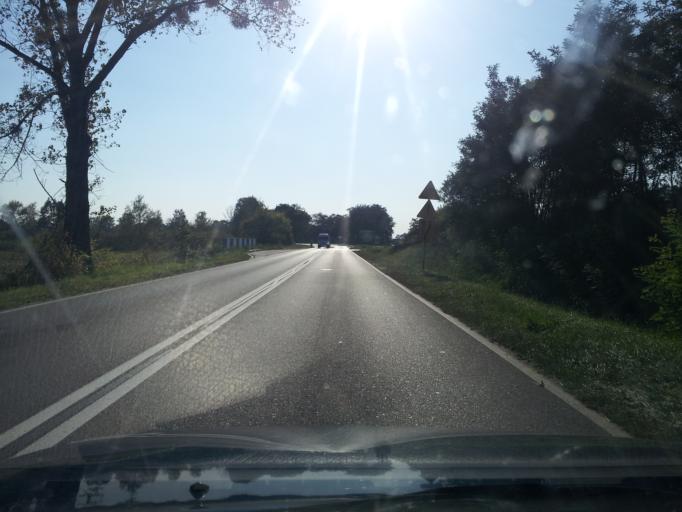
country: PL
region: Masovian Voivodeship
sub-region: Powiat nowodworski
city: Nowy Dwor Mazowiecki
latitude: 52.4039
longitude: 20.6854
